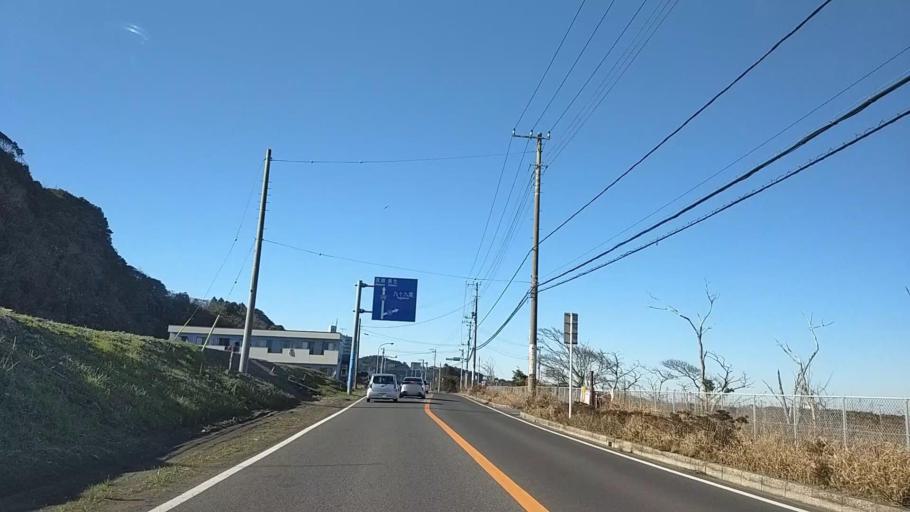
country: JP
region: Chiba
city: Ohara
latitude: 35.3322
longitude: 140.3938
